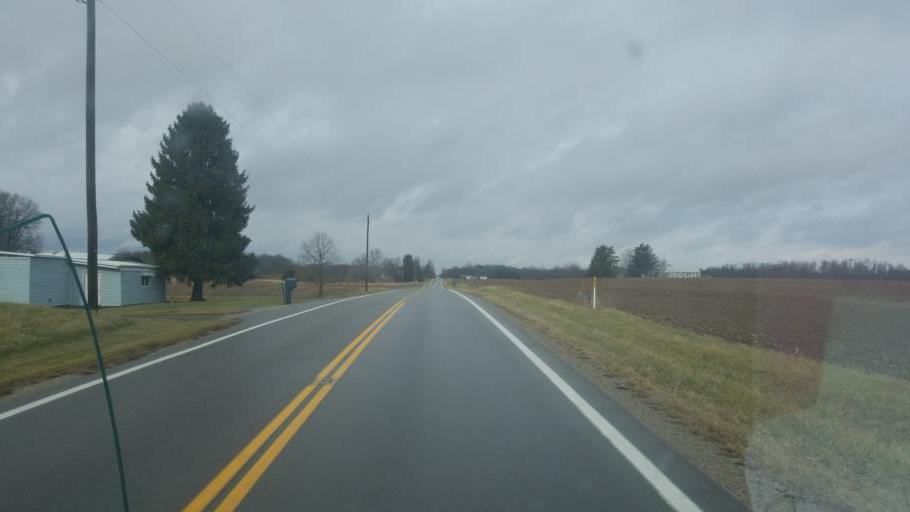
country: US
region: Ohio
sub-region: Crawford County
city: Bucyrus
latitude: 40.7597
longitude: -83.1308
